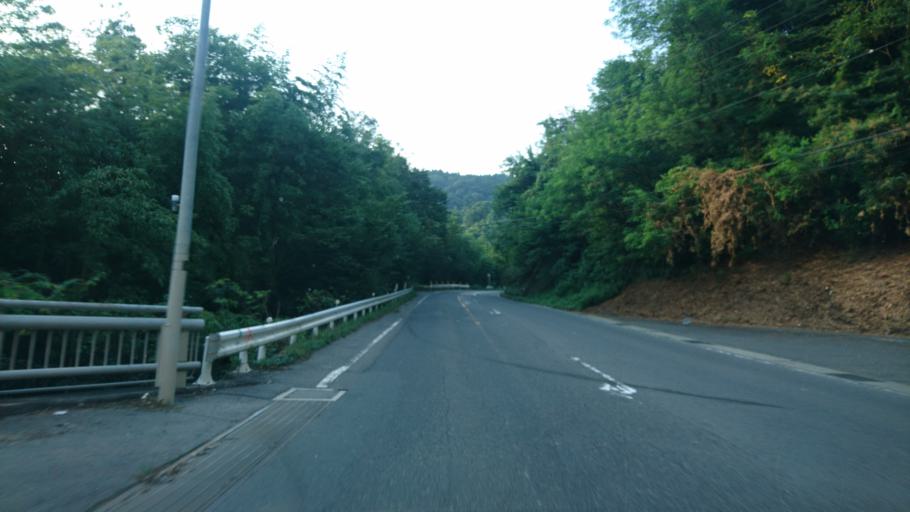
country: JP
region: Gunma
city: Numata
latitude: 36.6469
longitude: 139.1619
